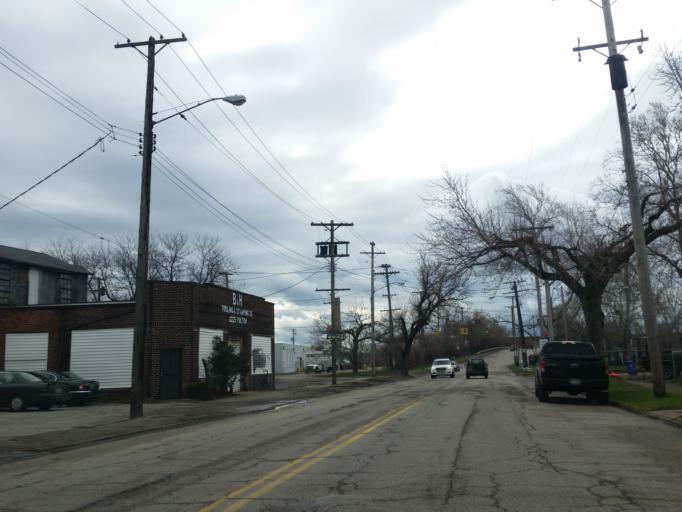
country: US
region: Ohio
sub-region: Cuyahoga County
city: Cleveland
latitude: 41.4786
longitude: -81.7094
